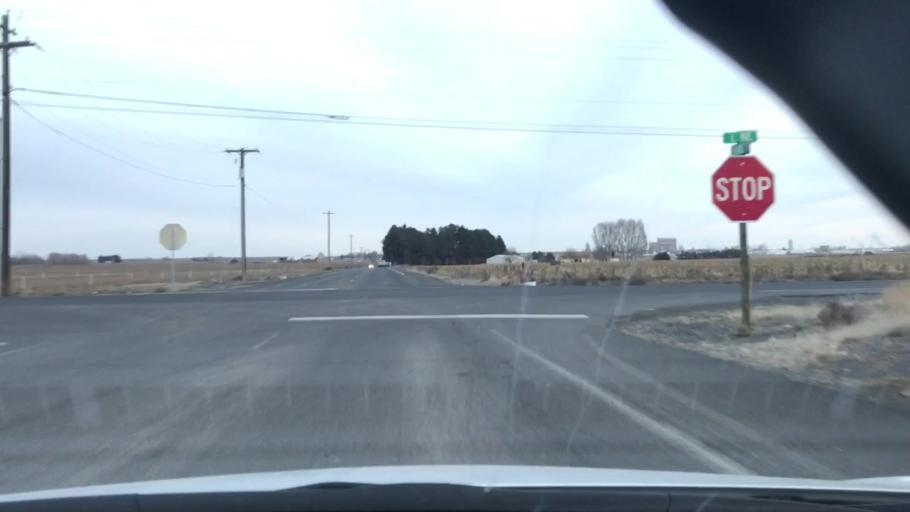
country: US
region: Washington
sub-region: Grant County
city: Moses Lake
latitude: 47.1455
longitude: -119.2360
